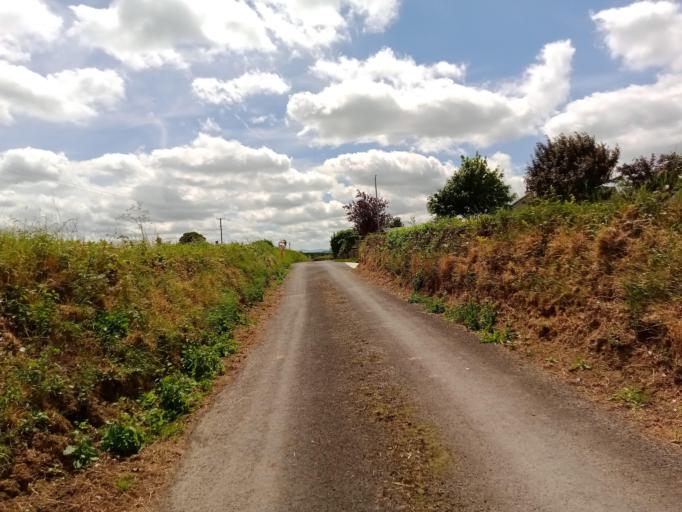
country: IE
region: Leinster
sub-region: Kilkenny
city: Callan
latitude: 52.5475
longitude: -7.4191
